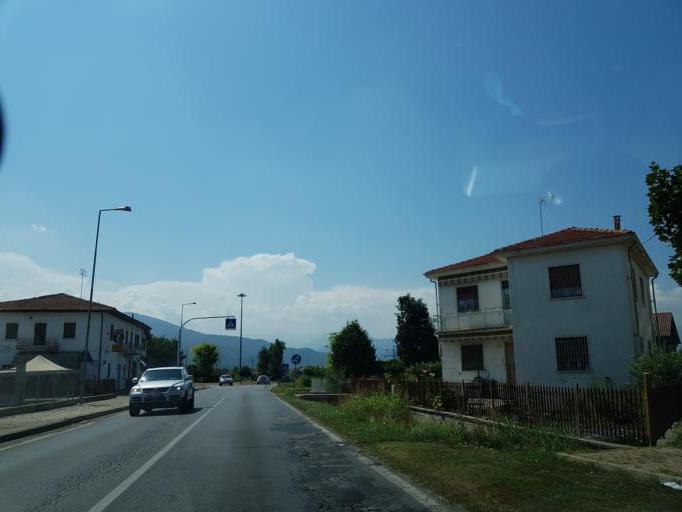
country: IT
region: Piedmont
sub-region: Provincia di Cuneo
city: San Rocco
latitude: 44.3980
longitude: 7.4735
